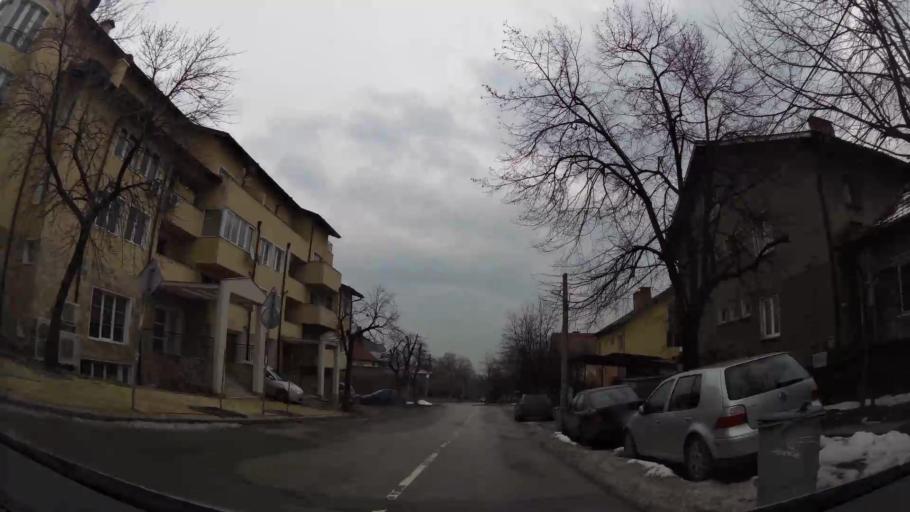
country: BG
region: Sofiya
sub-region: Obshtina Bozhurishte
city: Bozhurishte
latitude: 42.6754
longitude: 23.2348
